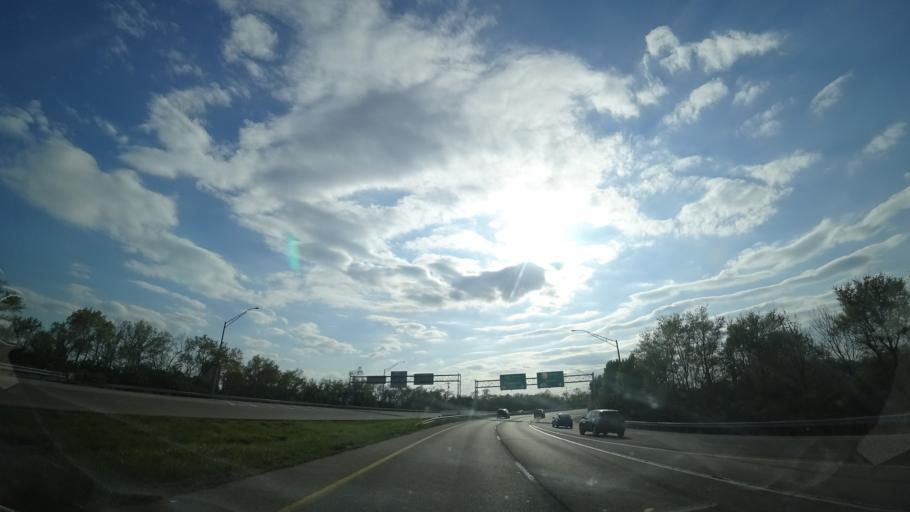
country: US
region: Ohio
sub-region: Montgomery County
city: Dayton
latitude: 39.7711
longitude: -84.1815
